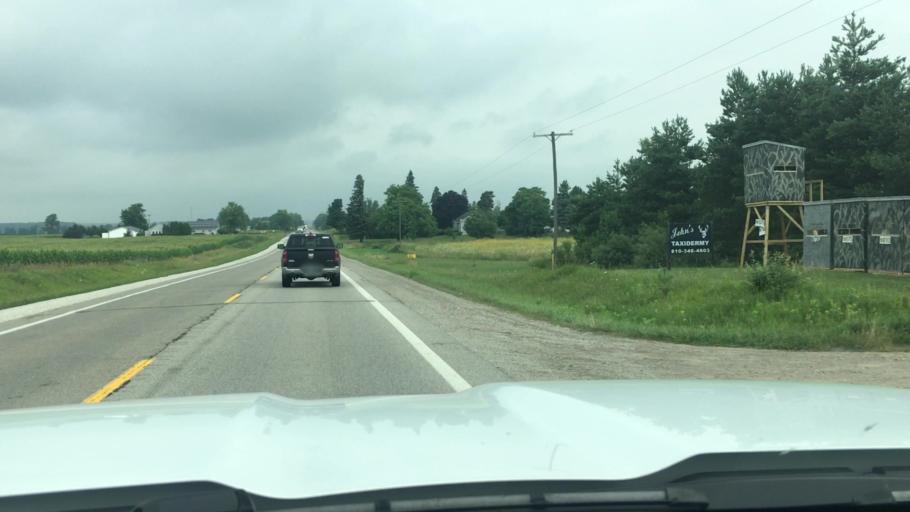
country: US
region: Michigan
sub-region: Sanilac County
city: Brown City
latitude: 43.1911
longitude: -83.0766
